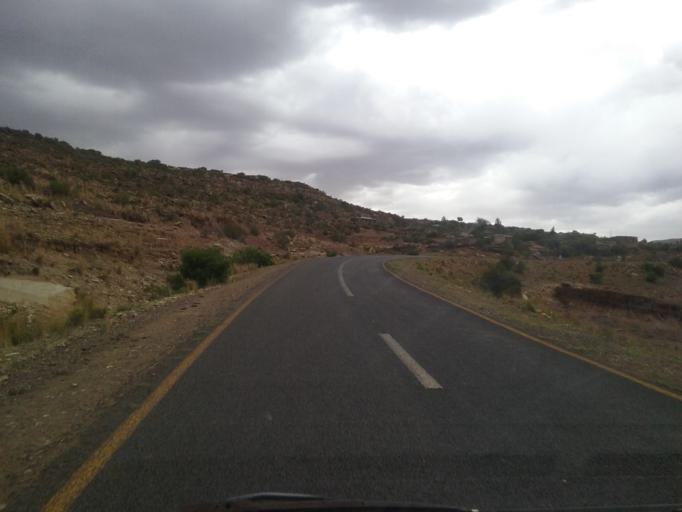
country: LS
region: Quthing
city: Quthing
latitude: -30.2915
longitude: 27.8096
